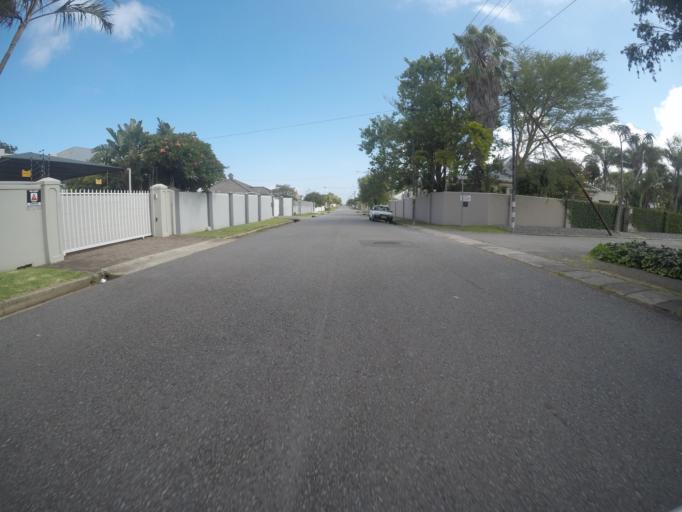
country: ZA
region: Eastern Cape
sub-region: Buffalo City Metropolitan Municipality
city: East London
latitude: -32.9797
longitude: 27.9072
